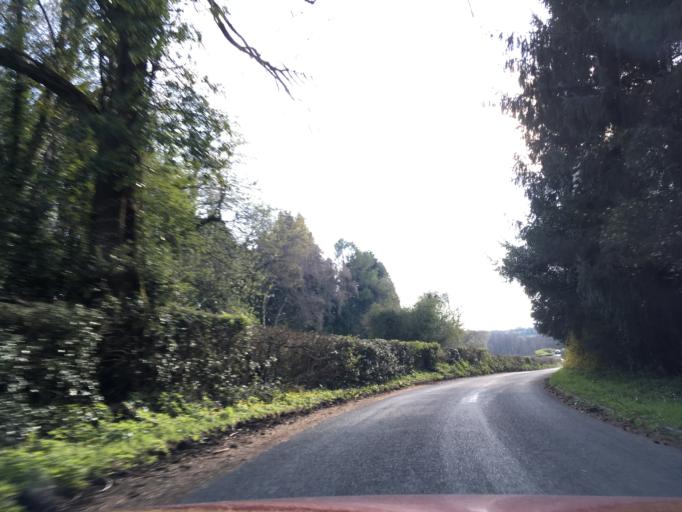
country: GB
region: Wales
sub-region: Monmouthshire
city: Usk
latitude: 51.7168
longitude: -2.9545
